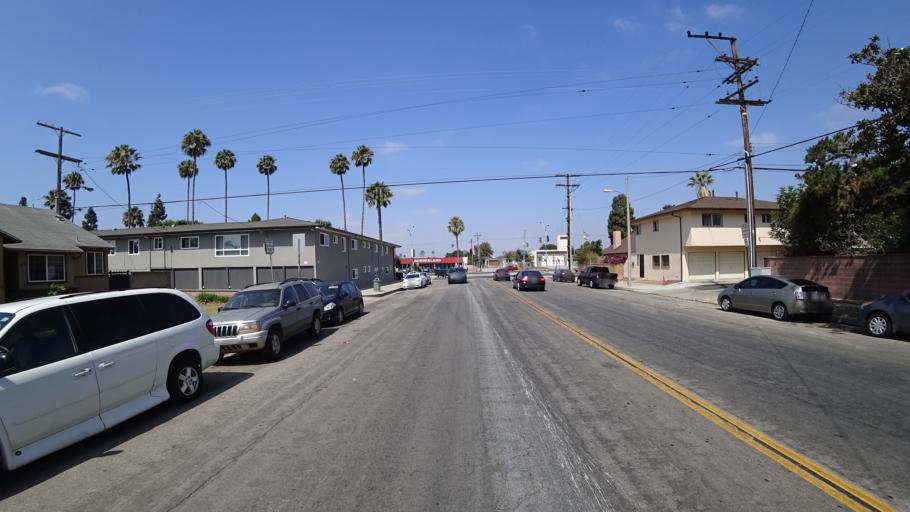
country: US
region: California
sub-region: Los Angeles County
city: Westmont
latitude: 33.9382
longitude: -118.3256
